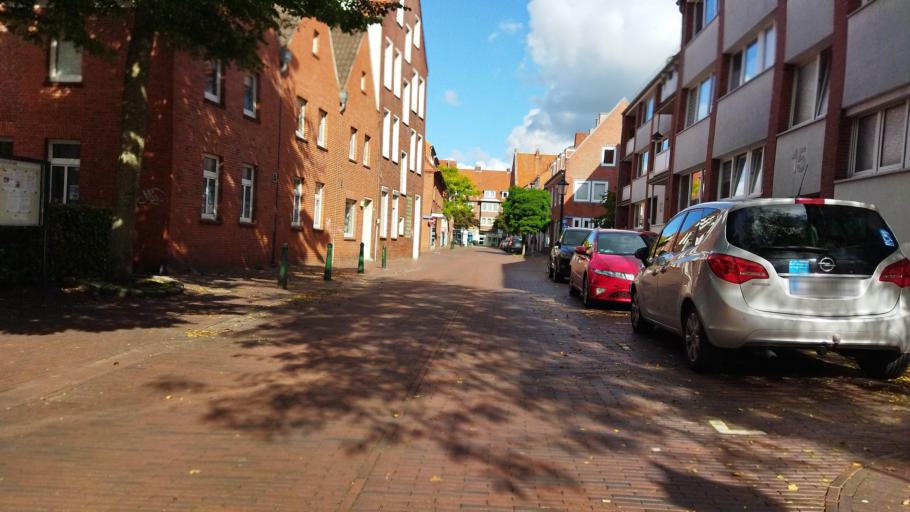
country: DE
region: Lower Saxony
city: Emden
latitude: 53.3657
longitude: 7.2028
